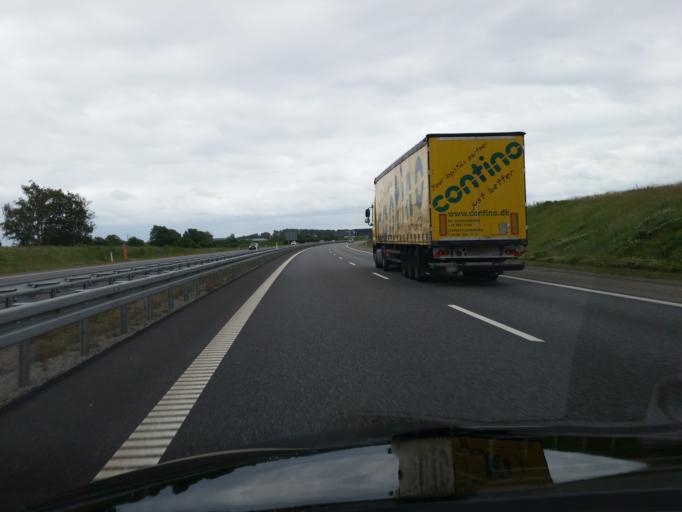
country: DK
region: South Denmark
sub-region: Vejle Kommune
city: Vejle
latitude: 55.7552
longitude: 9.5757
